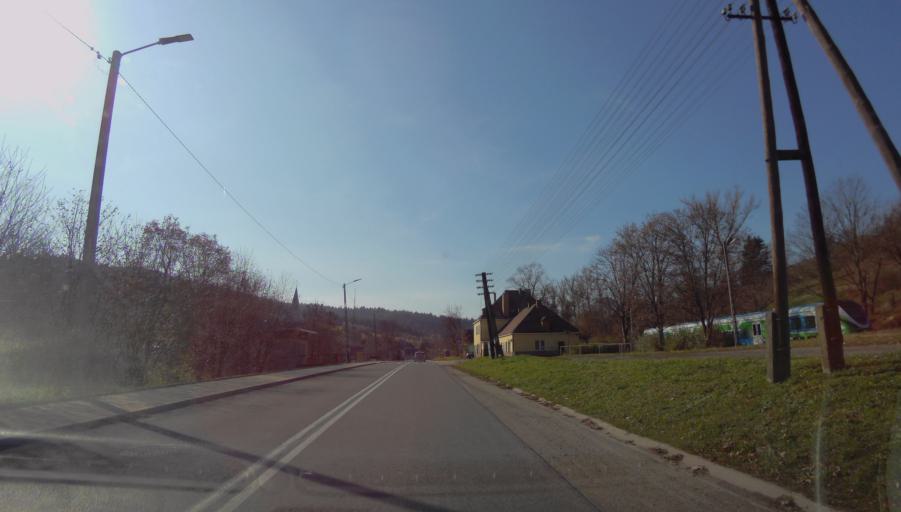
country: PL
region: Subcarpathian Voivodeship
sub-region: Powiat sanocki
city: Komancza
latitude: 49.3394
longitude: 22.0733
